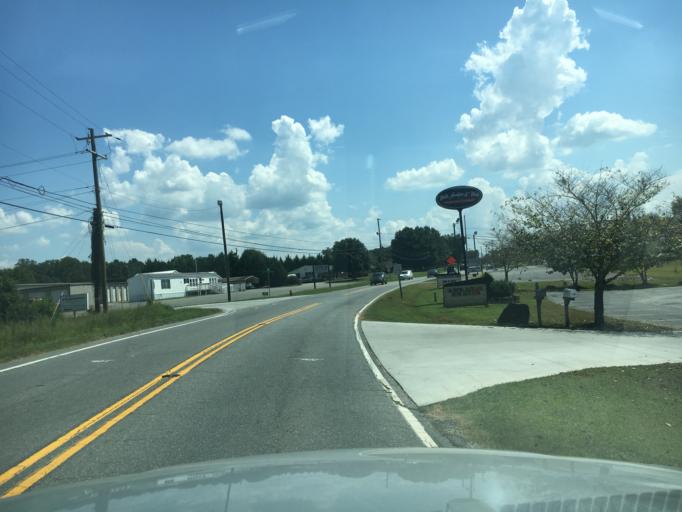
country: US
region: North Carolina
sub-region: Rutherford County
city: Forest City
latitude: 35.2982
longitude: -81.8479
